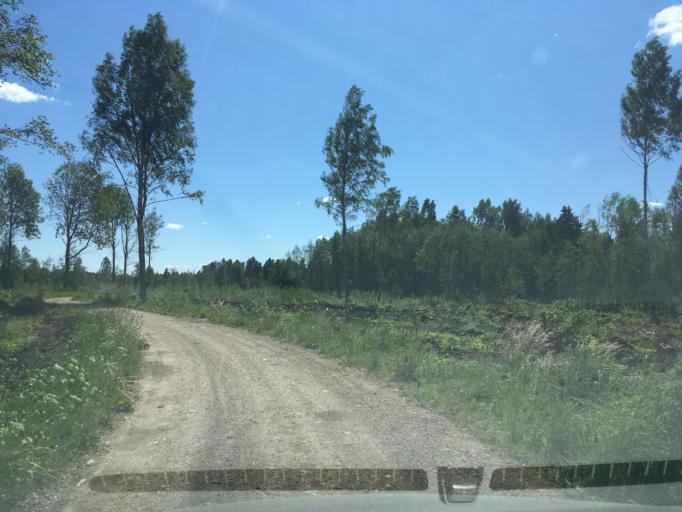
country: EE
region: Harju
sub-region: Raasiku vald
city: Raasiku
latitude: 59.1550
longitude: 25.1443
